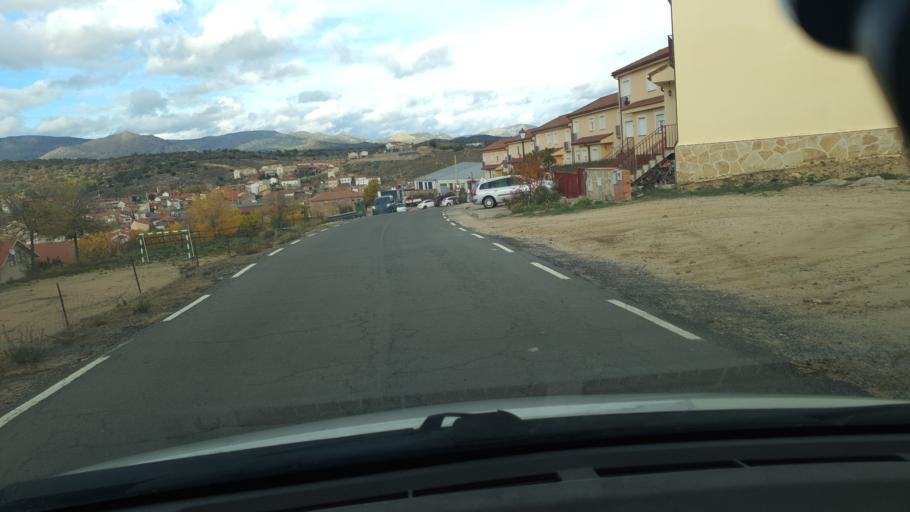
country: ES
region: Castille and Leon
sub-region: Provincia de Avila
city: Burgohondo
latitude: 40.4093
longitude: -4.7877
